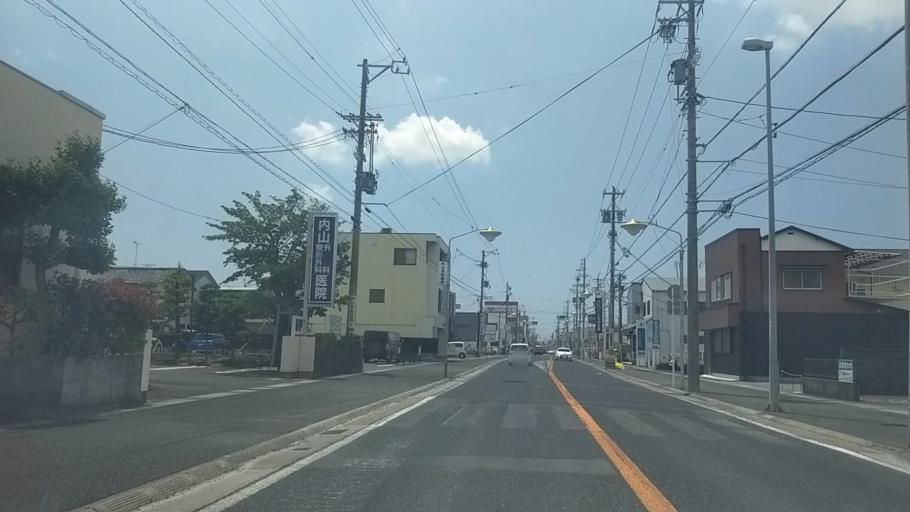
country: JP
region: Shizuoka
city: Hamamatsu
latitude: 34.7460
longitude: 137.7242
